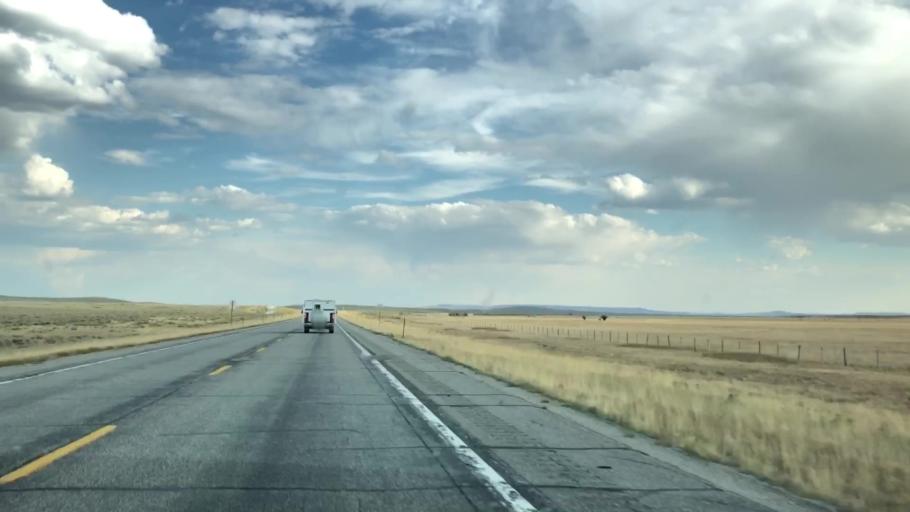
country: US
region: Wyoming
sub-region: Sublette County
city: Pinedale
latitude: 43.0416
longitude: -110.1408
